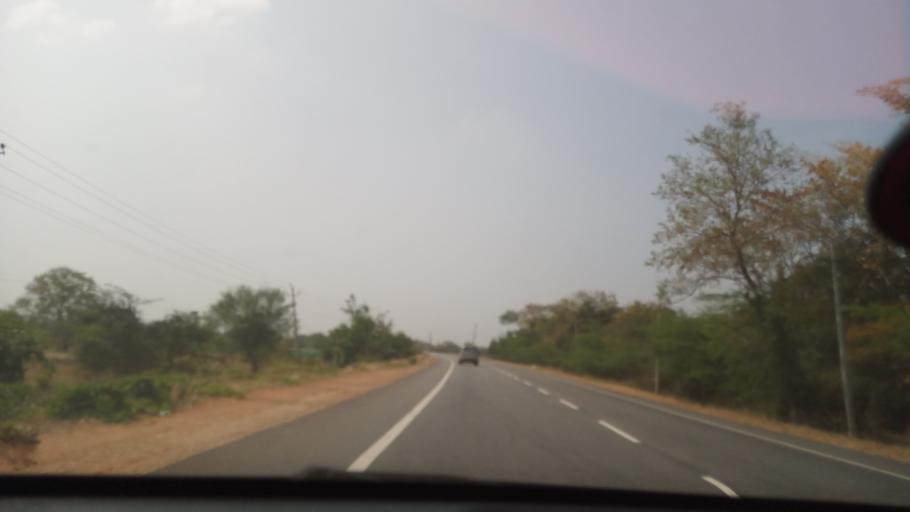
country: IN
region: Karnataka
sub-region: Mysore
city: Nanjangud
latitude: 12.0631
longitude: 76.7576
